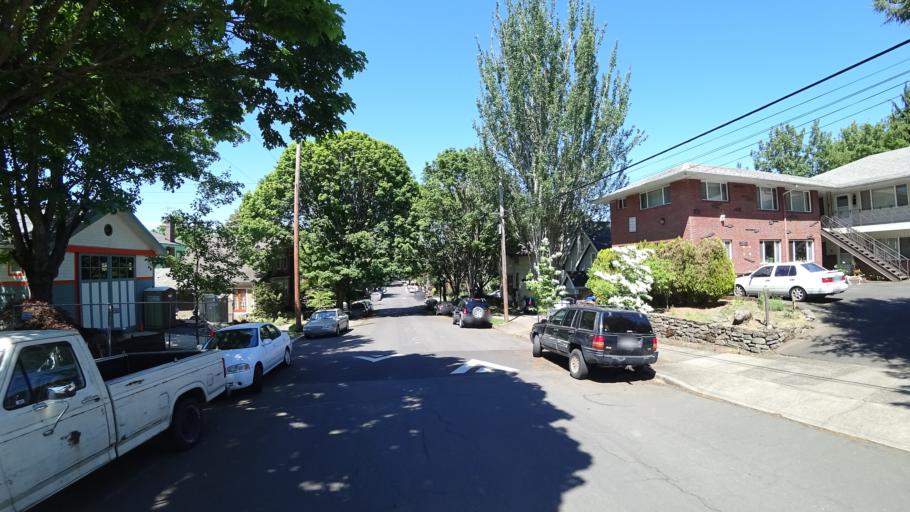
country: US
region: Oregon
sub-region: Multnomah County
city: Portland
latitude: 45.5153
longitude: -122.6361
